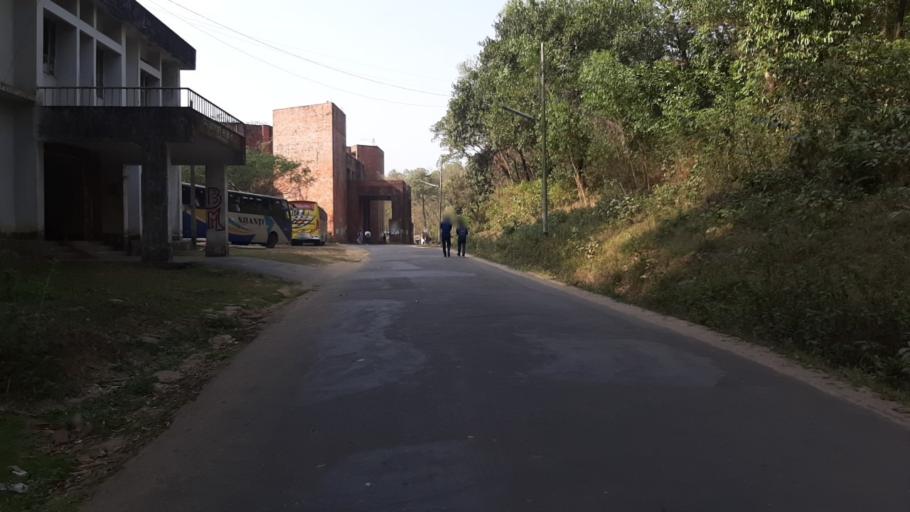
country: BD
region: Chittagong
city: Raojan
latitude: 22.4748
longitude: 91.7917
